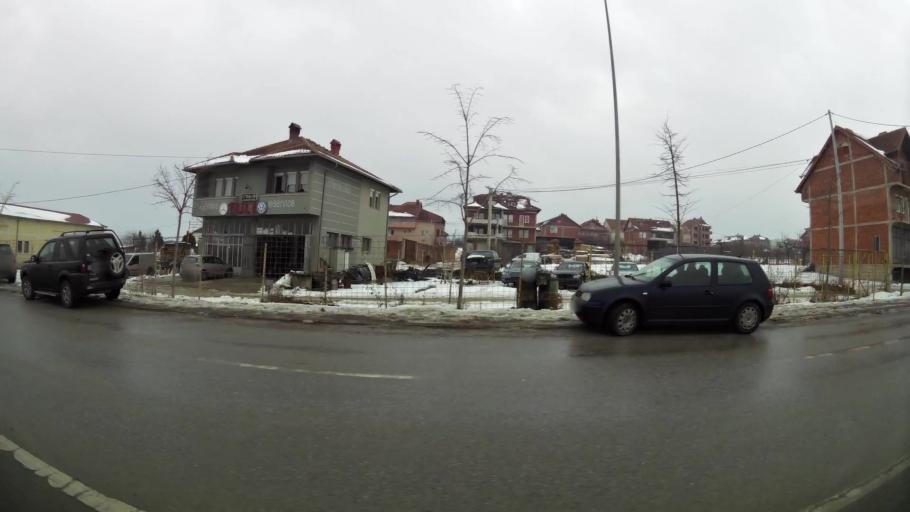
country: XK
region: Pristina
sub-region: Komuna e Prishtines
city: Pristina
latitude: 42.7002
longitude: 21.1590
